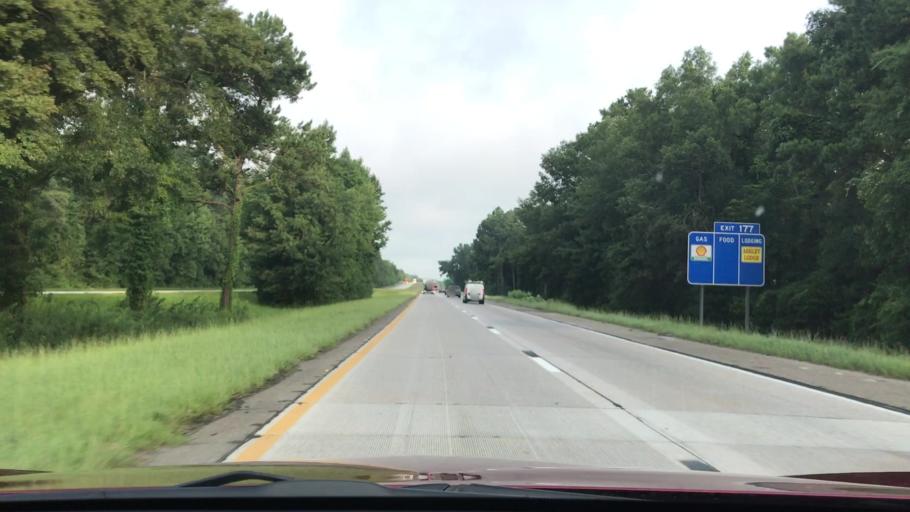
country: US
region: South Carolina
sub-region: Orangeburg County
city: Holly Hill
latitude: 33.2281
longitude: -80.4346
